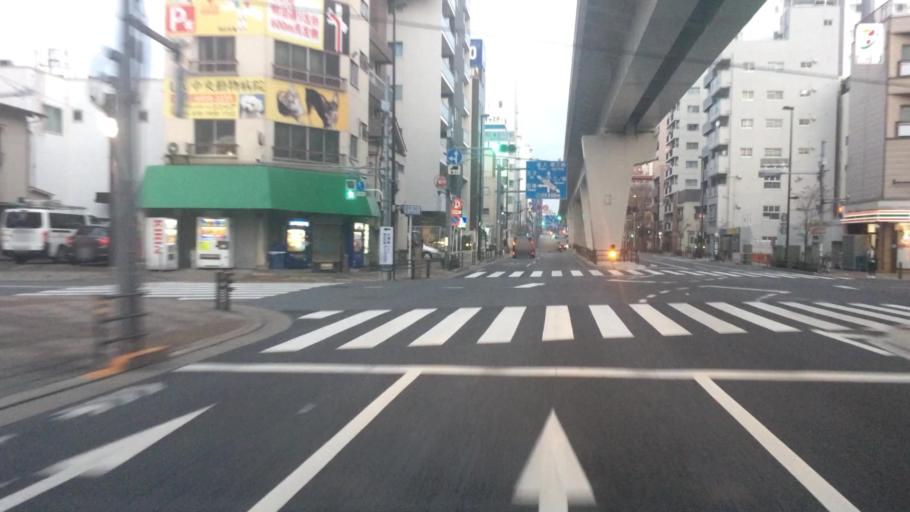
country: JP
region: Tokyo
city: Tokyo
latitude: 35.7362
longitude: 139.7684
